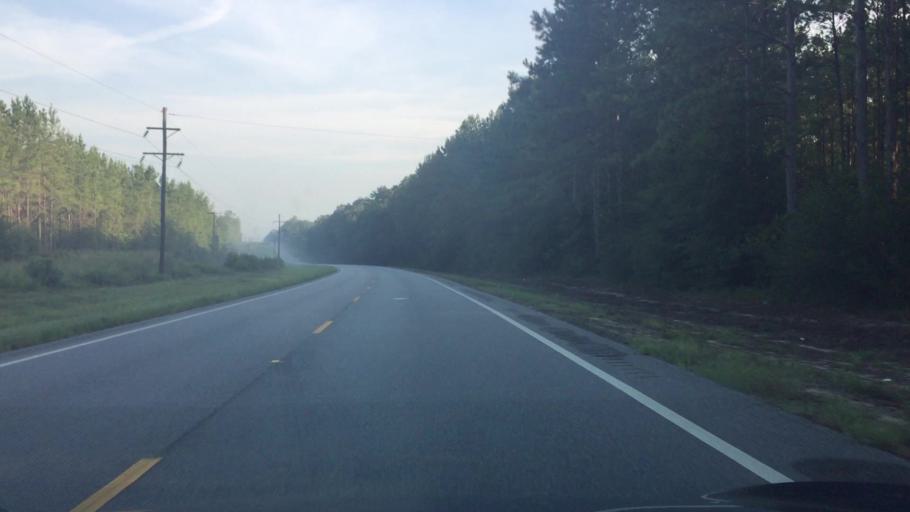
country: US
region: Alabama
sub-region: Covington County
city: Florala
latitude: 31.0572
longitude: -86.3918
